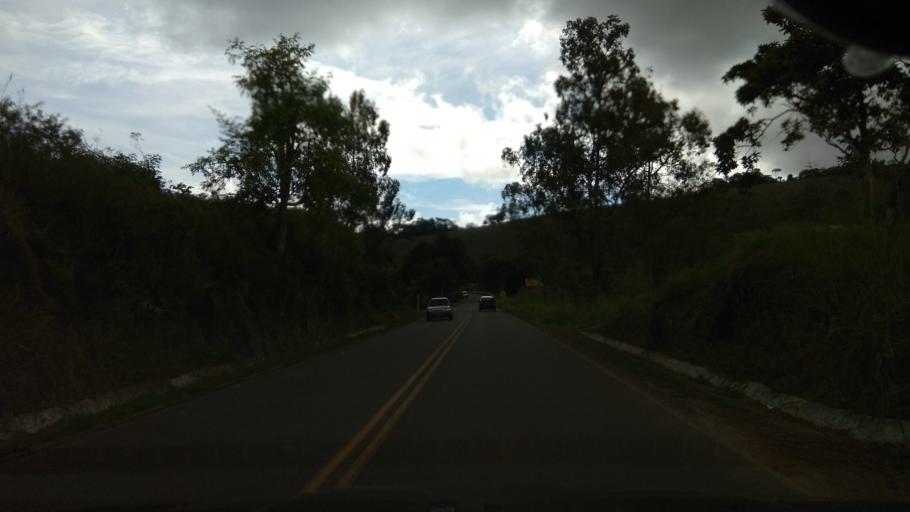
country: BR
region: Bahia
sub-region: Mutuipe
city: Mutuipe
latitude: -13.2427
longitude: -39.5387
